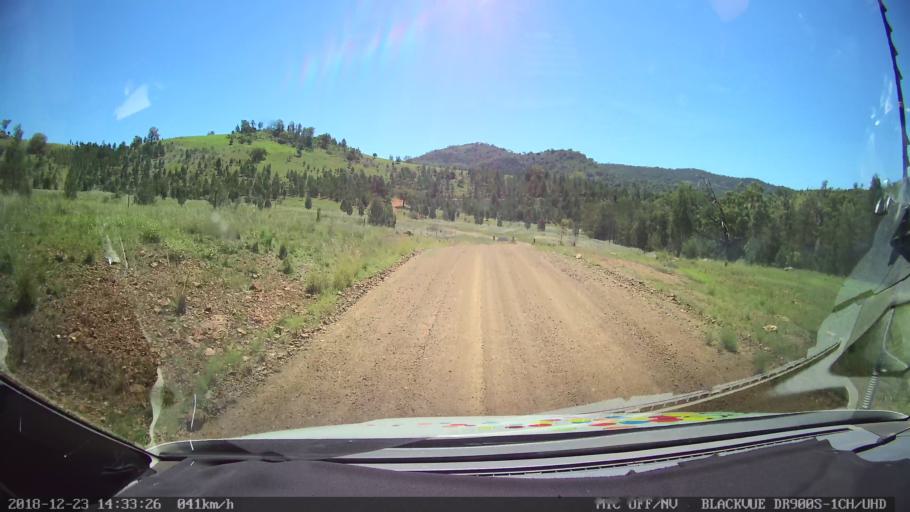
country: AU
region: New South Wales
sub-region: Tamworth Municipality
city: Manilla
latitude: -30.6077
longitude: 150.9139
